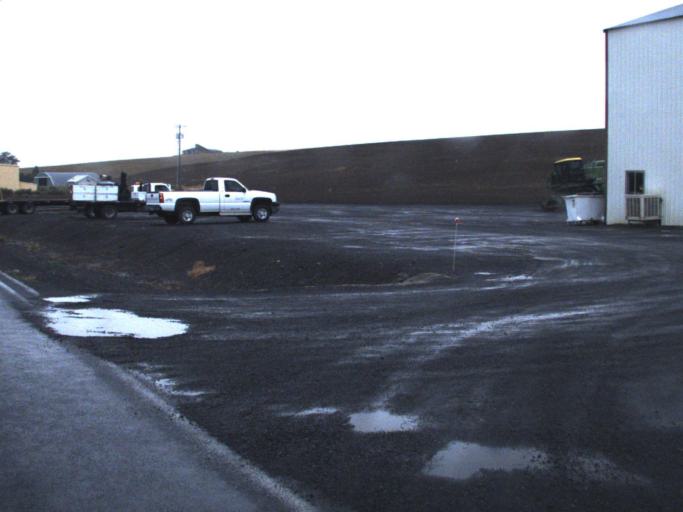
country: US
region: Washington
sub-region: Whitman County
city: Colfax
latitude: 47.0916
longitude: -117.5740
